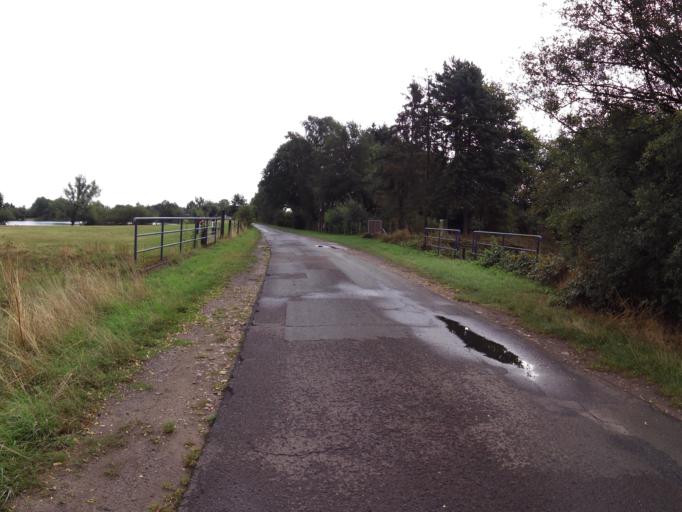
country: DE
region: Lower Saxony
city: Marklohe
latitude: 52.6878
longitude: 9.1726
